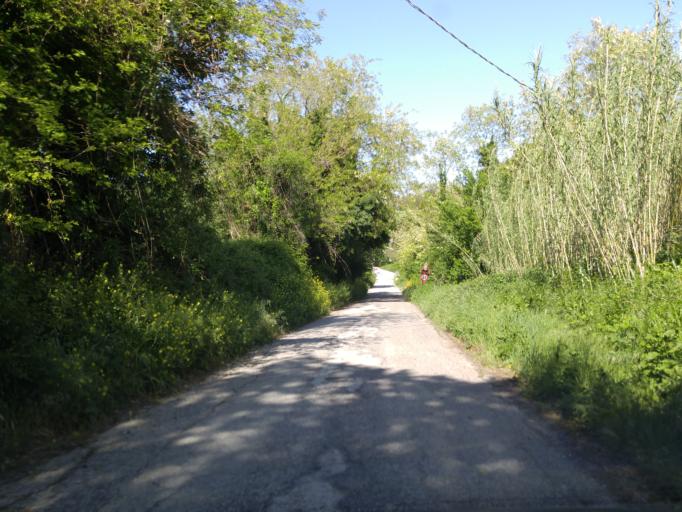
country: IT
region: The Marches
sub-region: Provincia di Pesaro e Urbino
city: Cartoceto
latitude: 43.7816
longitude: 12.9033
